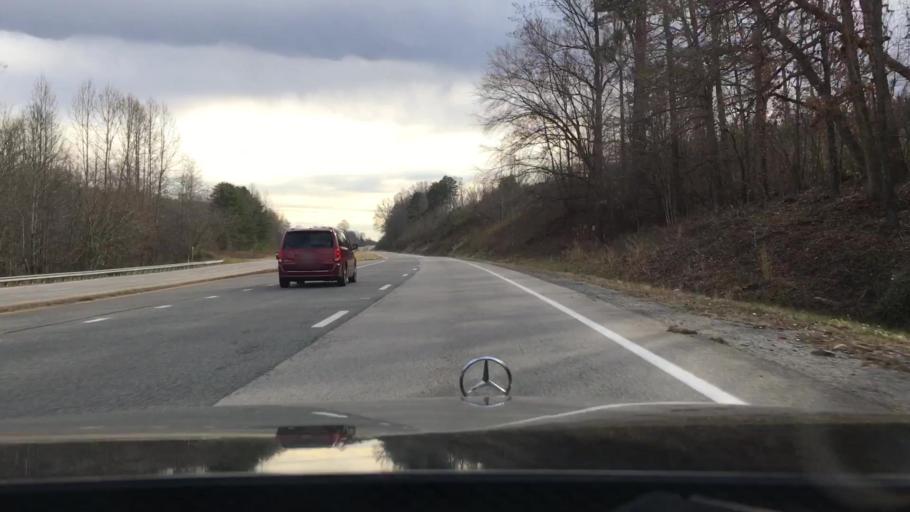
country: US
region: Virginia
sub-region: Pittsylvania County
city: Motley
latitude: 37.0166
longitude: -79.3576
